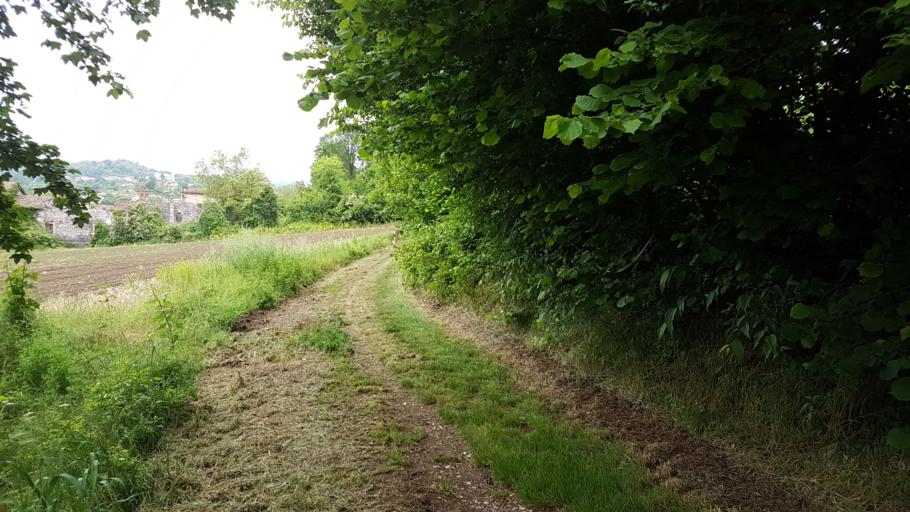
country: IT
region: Veneto
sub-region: Provincia di Vicenza
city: Tezze
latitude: 45.5485
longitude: 11.3418
